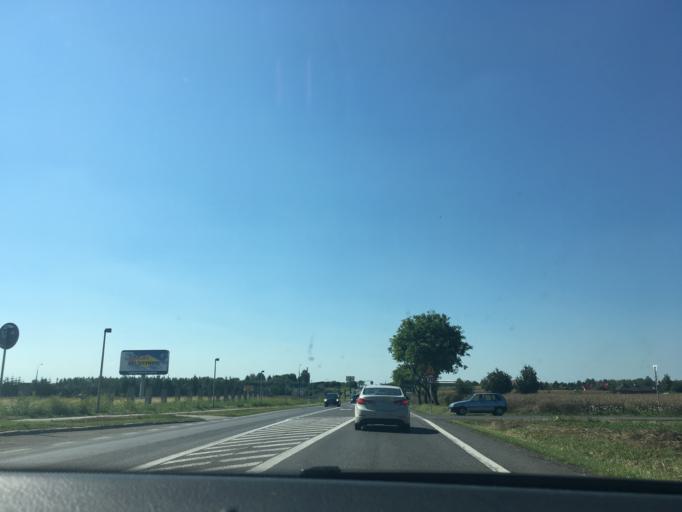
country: PL
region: Lublin Voivodeship
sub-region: Powiat lubelski
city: Niemce
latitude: 51.3449
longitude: 22.6191
